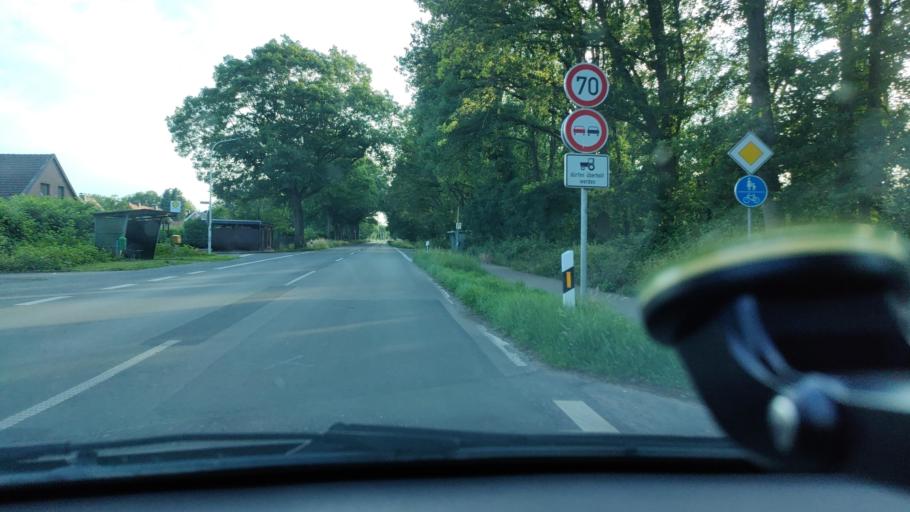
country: DE
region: North Rhine-Westphalia
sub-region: Regierungsbezirk Dusseldorf
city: Issum
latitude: 51.4999
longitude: 6.4439
